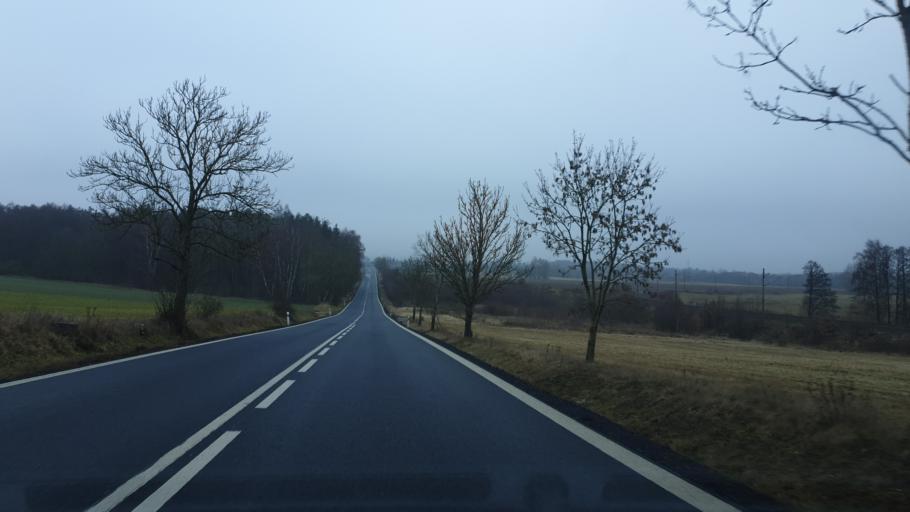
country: CZ
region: Karlovarsky
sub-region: Okres Cheb
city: Skalna
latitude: 50.1574
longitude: 12.3231
